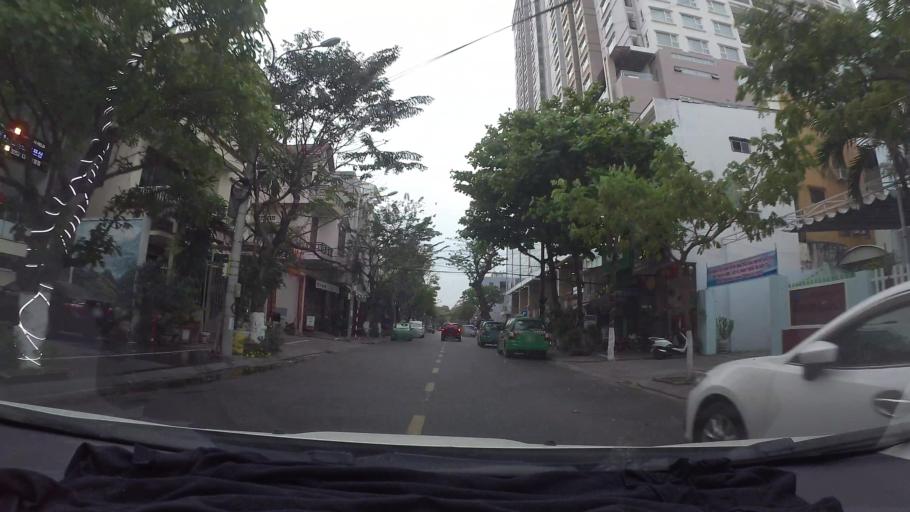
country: VN
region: Da Nang
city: Da Nang
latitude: 16.0802
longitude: 108.2210
